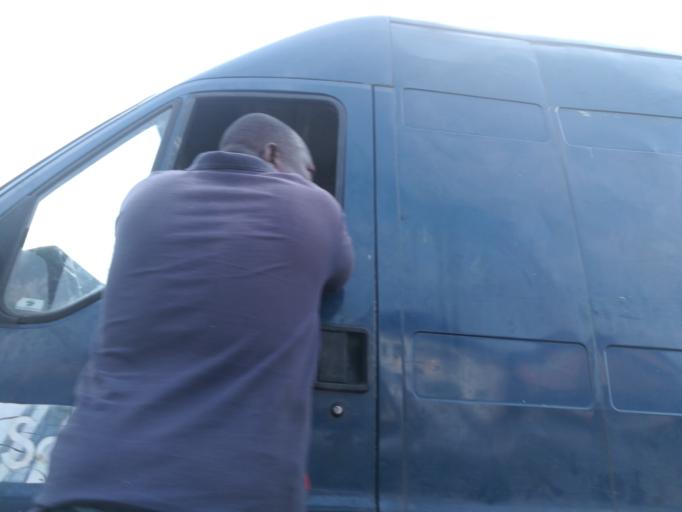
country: NG
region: Rivers
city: Okrika
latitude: 4.7425
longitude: 7.0905
